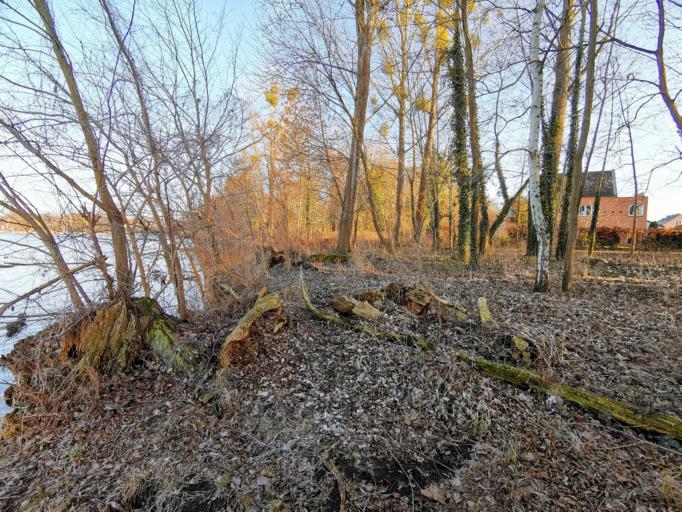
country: DE
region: Brandenburg
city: Potsdam
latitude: 52.3873
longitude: 13.0373
